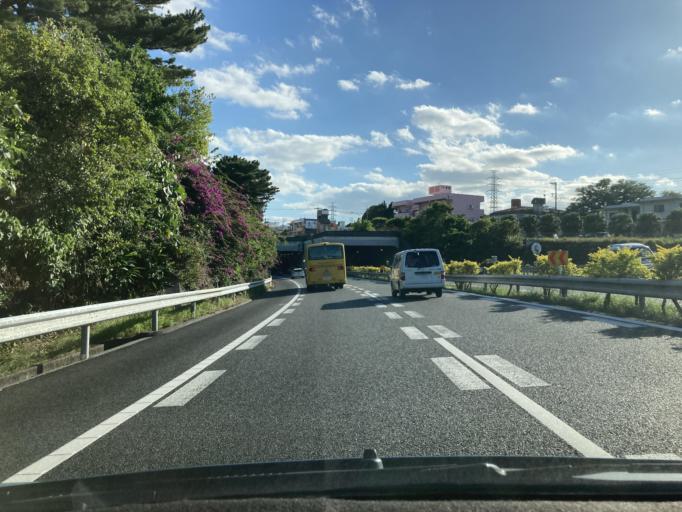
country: JP
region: Okinawa
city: Okinawa
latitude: 26.3324
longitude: 127.7836
